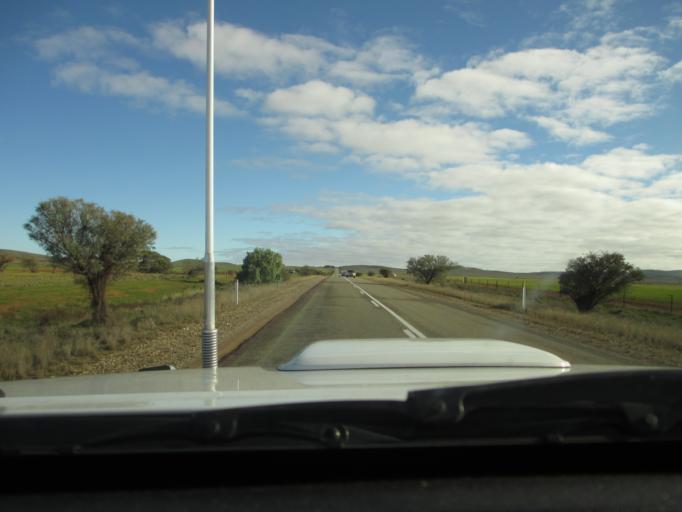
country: AU
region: South Australia
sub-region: Peterborough
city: Peterborough
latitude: -32.6341
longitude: 138.5949
